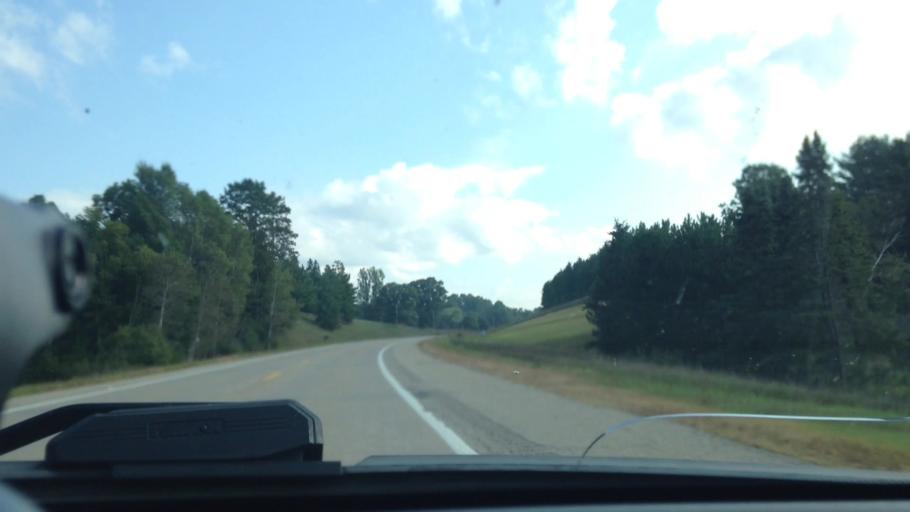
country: US
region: Michigan
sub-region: Dickinson County
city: Norway
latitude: 45.7633
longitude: -87.9196
